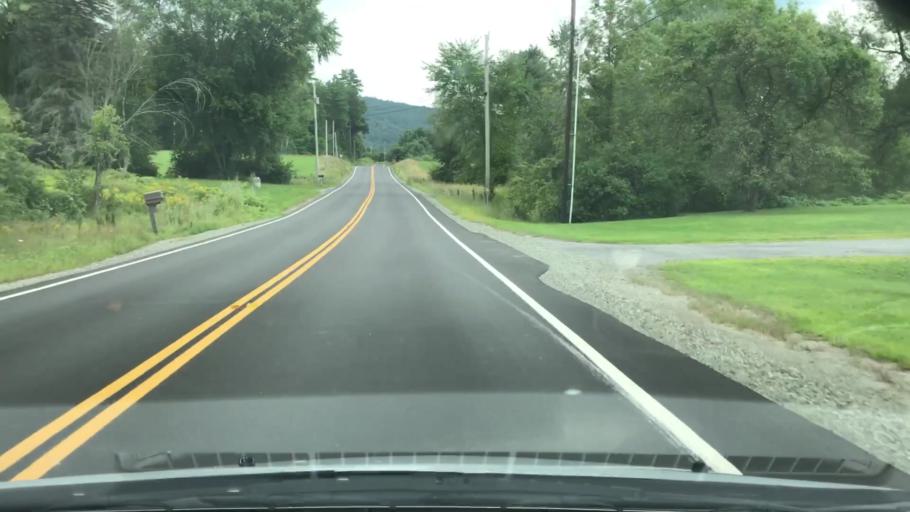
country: US
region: New Hampshire
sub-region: Grafton County
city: Lyme Town Offices
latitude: 43.8411
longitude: -72.1519
